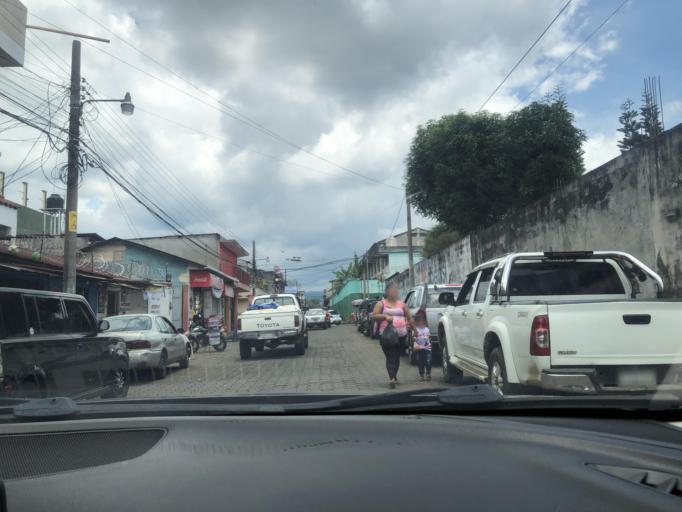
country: GT
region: Quetzaltenango
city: Coatepeque
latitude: 14.7062
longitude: -91.8648
